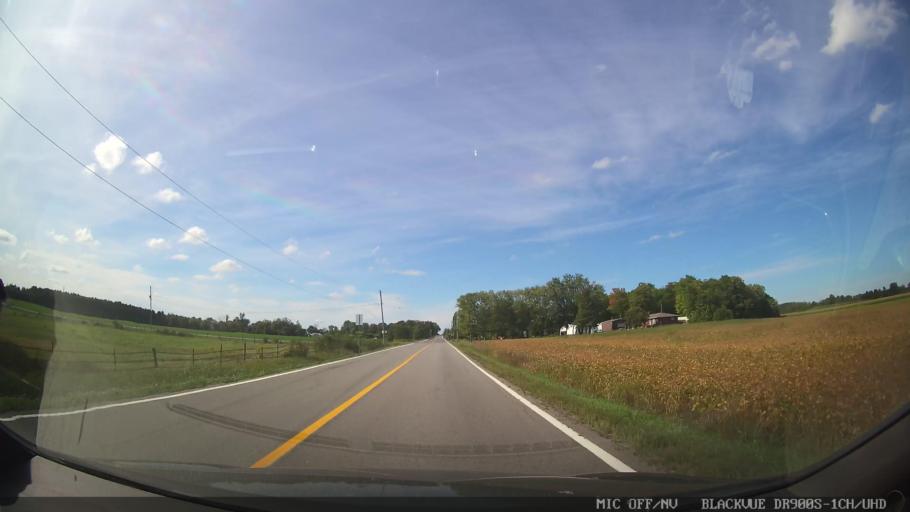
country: CA
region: Ontario
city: Bells Corners
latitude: 45.1001
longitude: -75.7113
